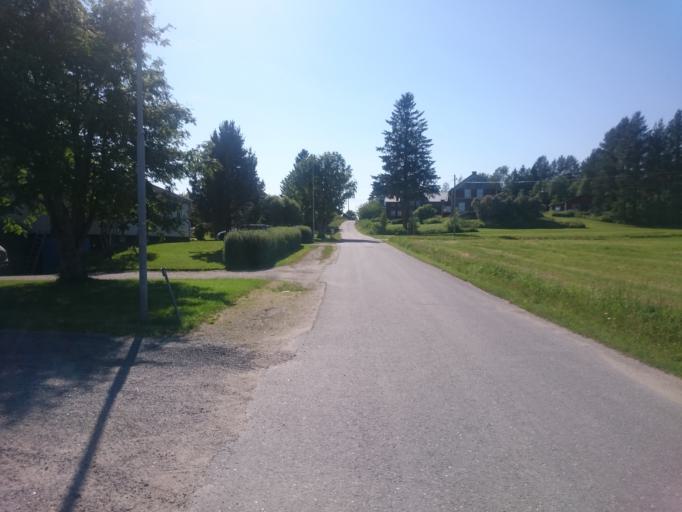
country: SE
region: Vaesternorrland
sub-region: OErnskoeldsviks Kommun
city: Bredbyn
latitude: 63.3002
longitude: 18.2722
